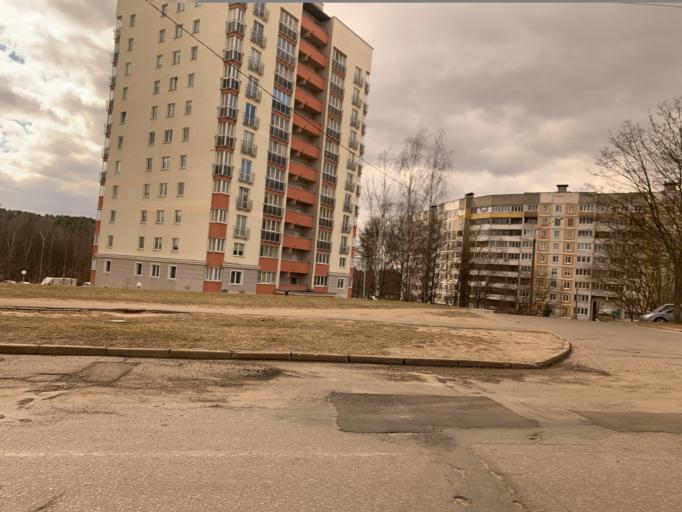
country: BY
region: Minsk
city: Borovlyany
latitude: 53.9340
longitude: 27.6890
